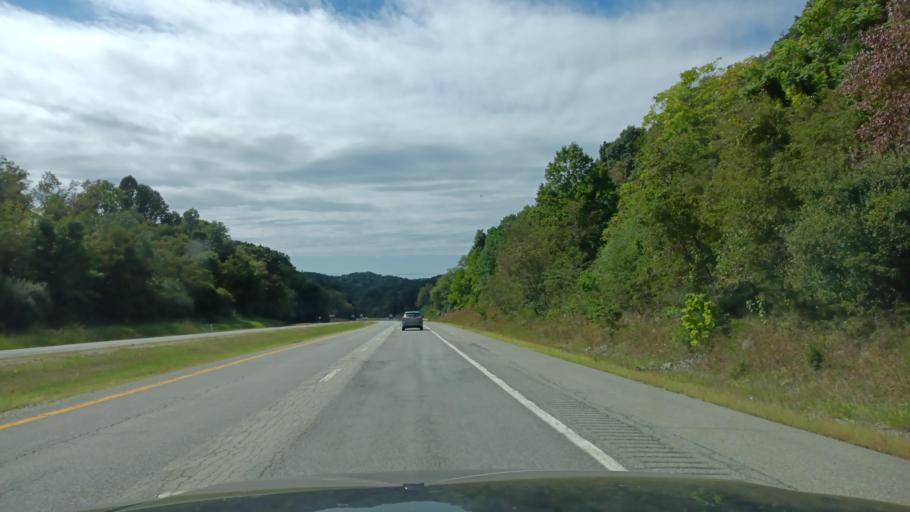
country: US
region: West Virginia
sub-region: Ritchie County
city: Harrisville
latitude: 39.2598
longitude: -81.1649
